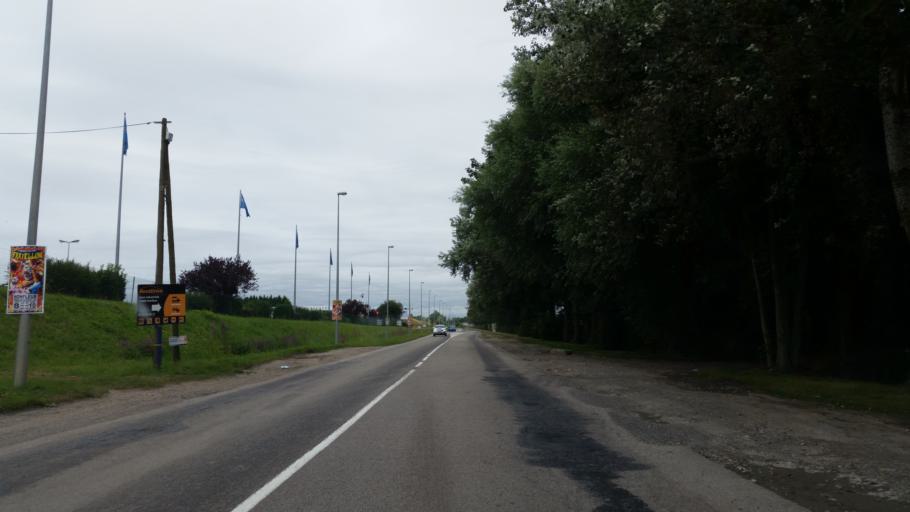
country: FR
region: Lower Normandy
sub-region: Departement du Calvados
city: La Riviere-Saint-Sauveur
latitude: 49.4147
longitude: 0.2593
